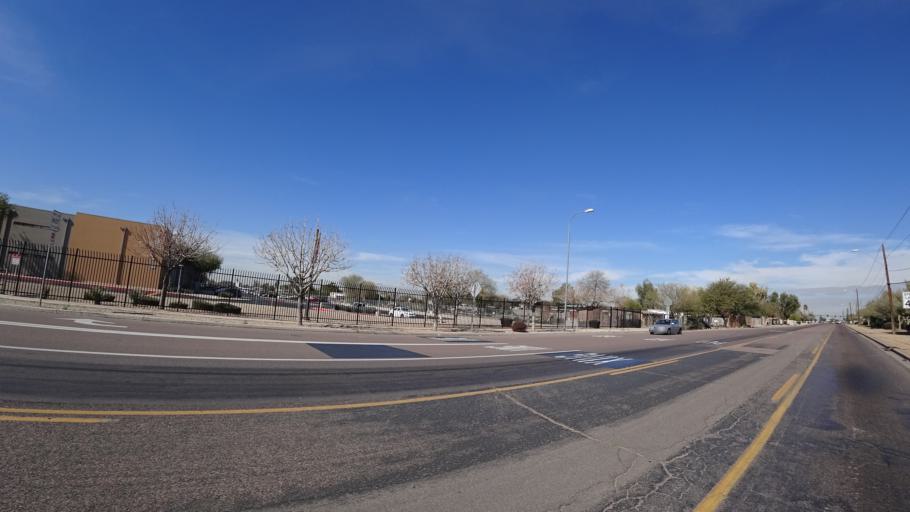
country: US
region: Arizona
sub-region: Maricopa County
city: Tolleson
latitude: 33.4191
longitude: -112.2040
